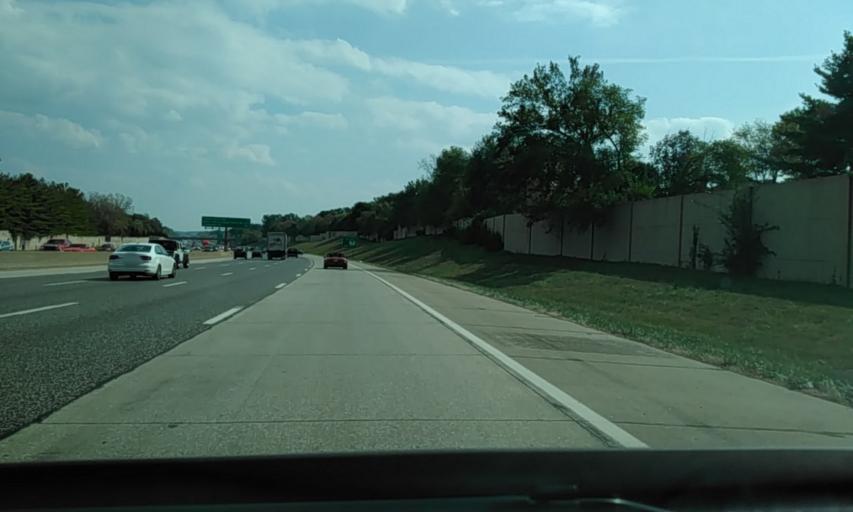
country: US
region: Missouri
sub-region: Saint Louis County
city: Sappington
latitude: 38.5181
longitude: -90.3891
